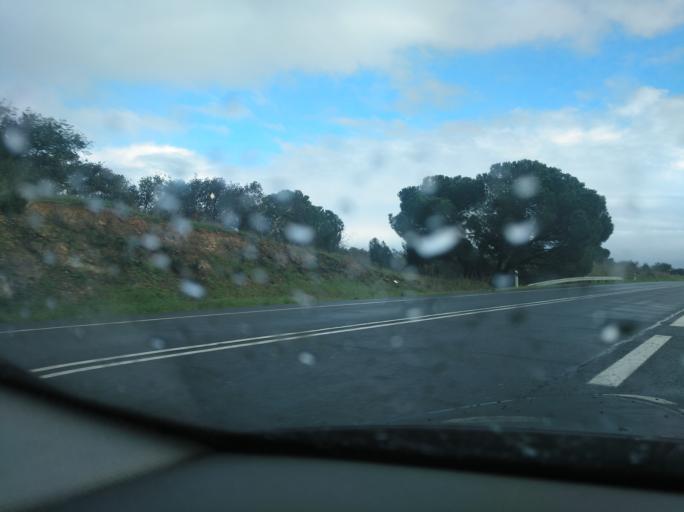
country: PT
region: Setubal
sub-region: Grandola
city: Grandola
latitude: 38.0599
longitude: -8.4070
